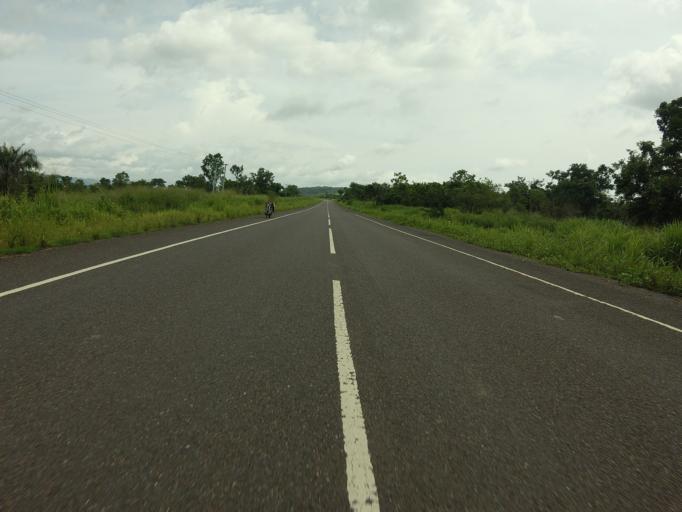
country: TG
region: Plateaux
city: Badou
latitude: 7.9622
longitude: 0.5563
